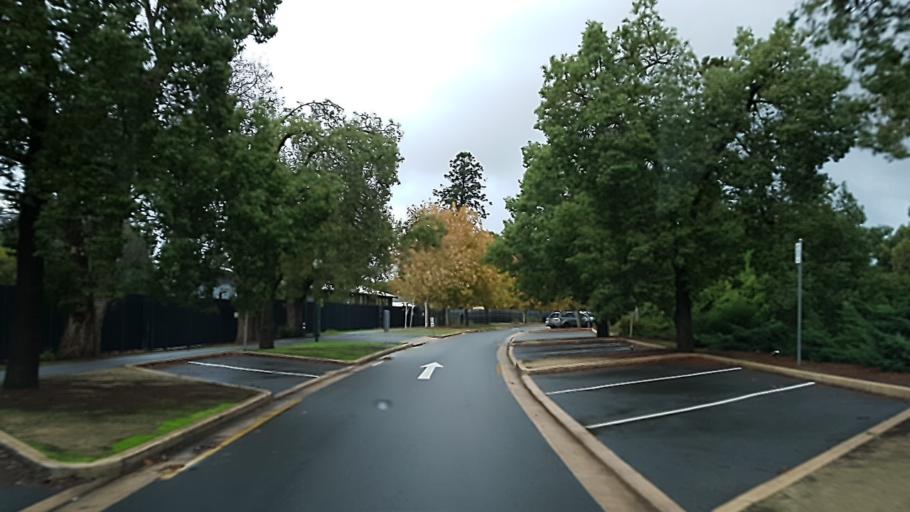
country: AU
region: South Australia
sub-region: Adelaide
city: Adelaide
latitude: -34.9140
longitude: 138.6074
